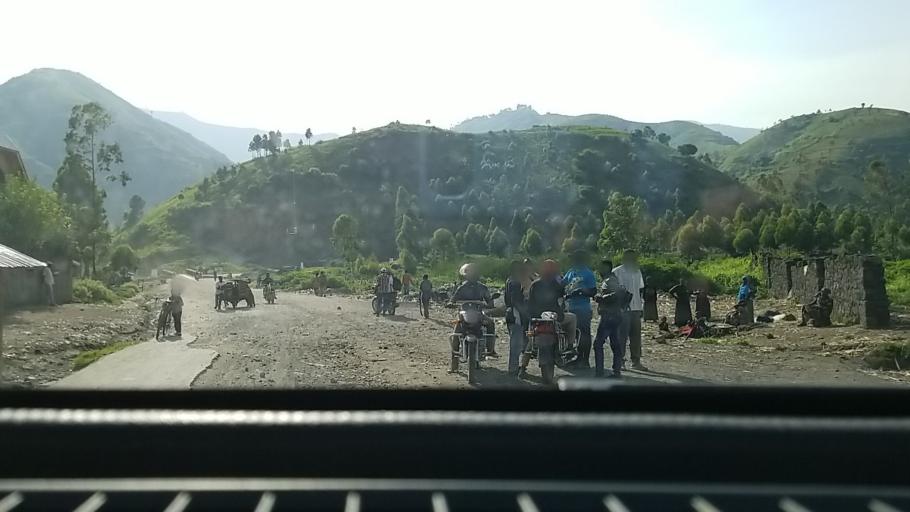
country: CD
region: Nord Kivu
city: Sake
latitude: -1.5710
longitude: 29.0479
